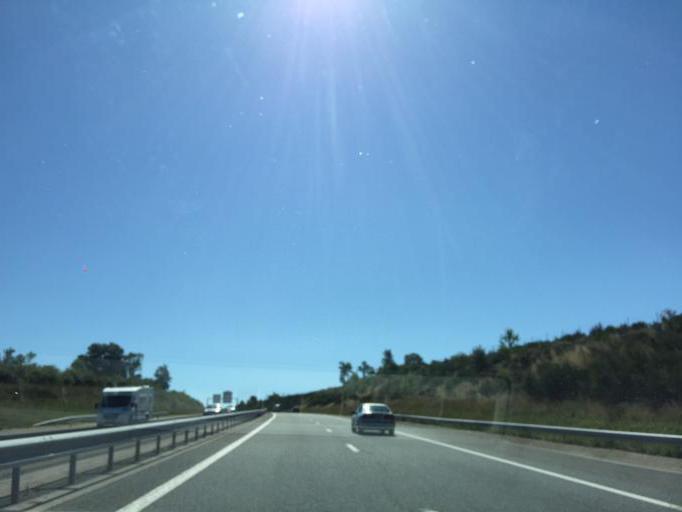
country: FR
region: Midi-Pyrenees
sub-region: Departement de l'Aveyron
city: La Cavalerie
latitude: 44.0029
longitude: 3.1520
